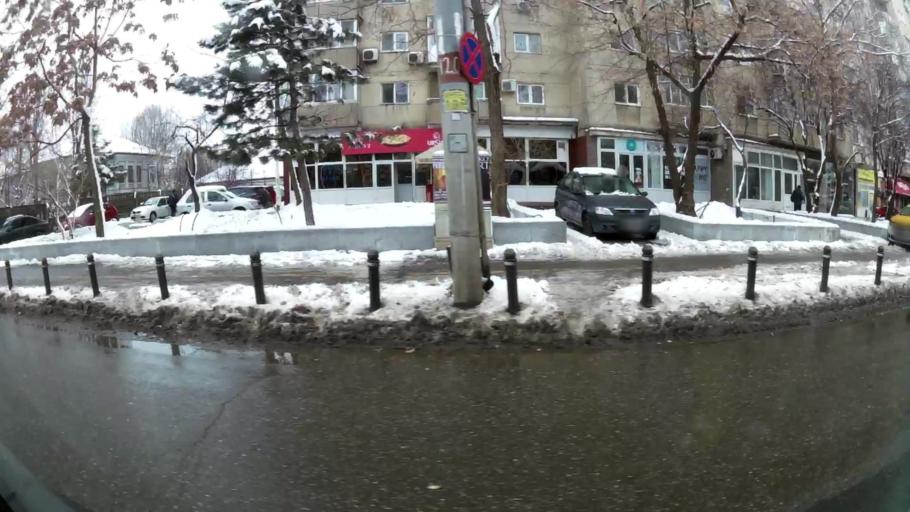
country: RO
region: Bucuresti
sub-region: Municipiul Bucuresti
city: Bucuresti
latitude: 44.3965
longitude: 26.1141
